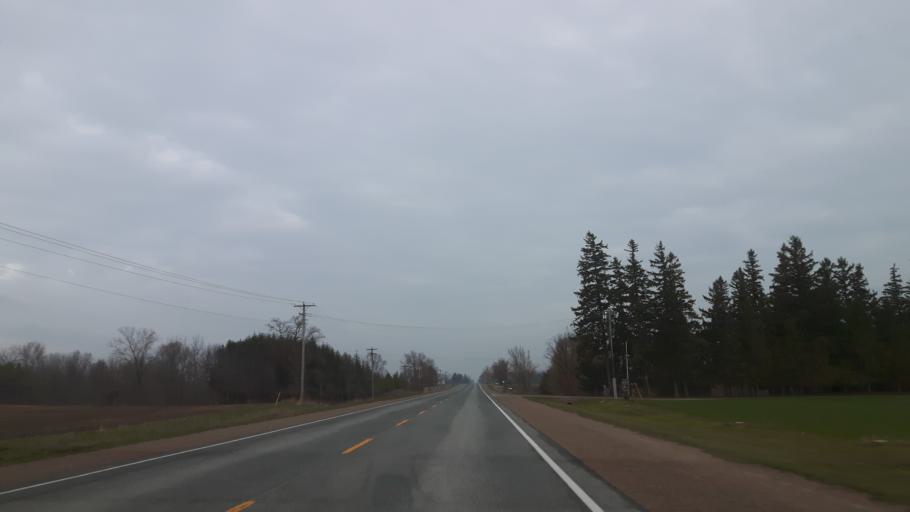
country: CA
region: Ontario
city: Bluewater
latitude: 43.5160
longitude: -81.6937
